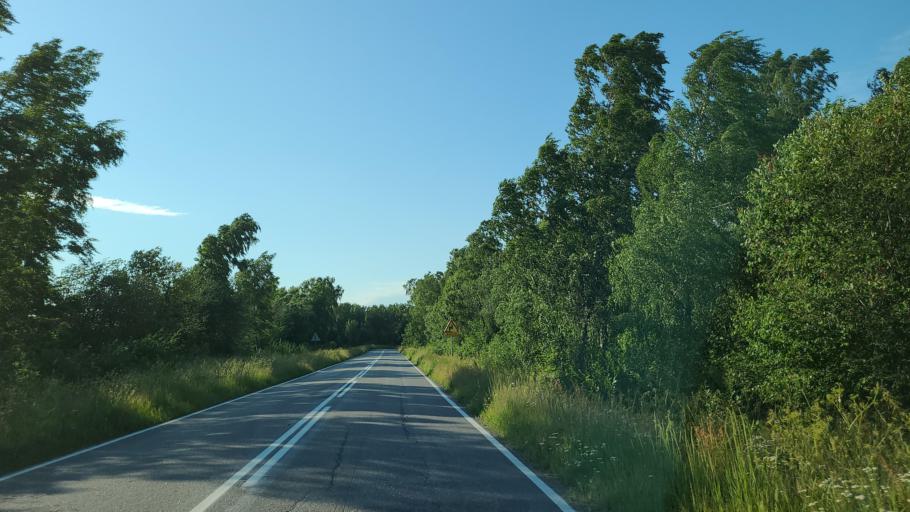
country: FI
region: Ostrobothnia
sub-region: Vaasa
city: Replot
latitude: 63.2836
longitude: 21.3352
